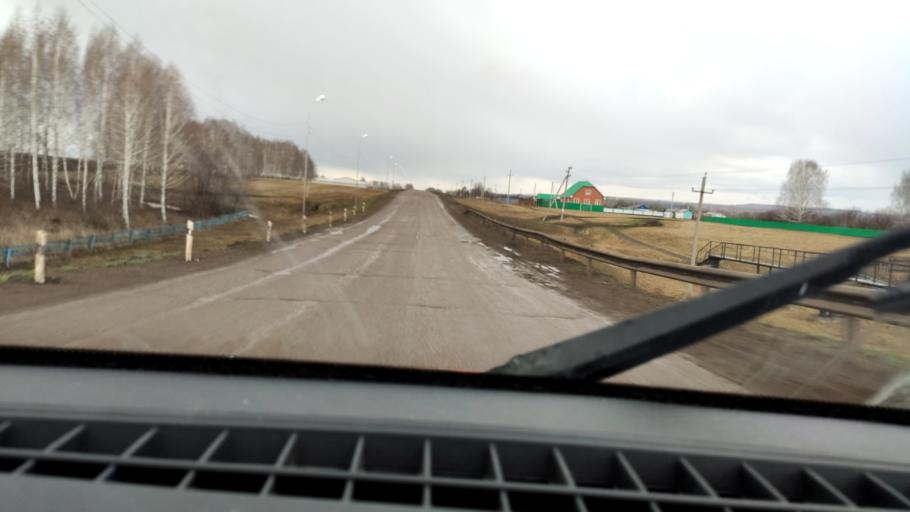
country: RU
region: Bashkortostan
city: Chekmagush
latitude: 55.1165
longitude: 54.8350
